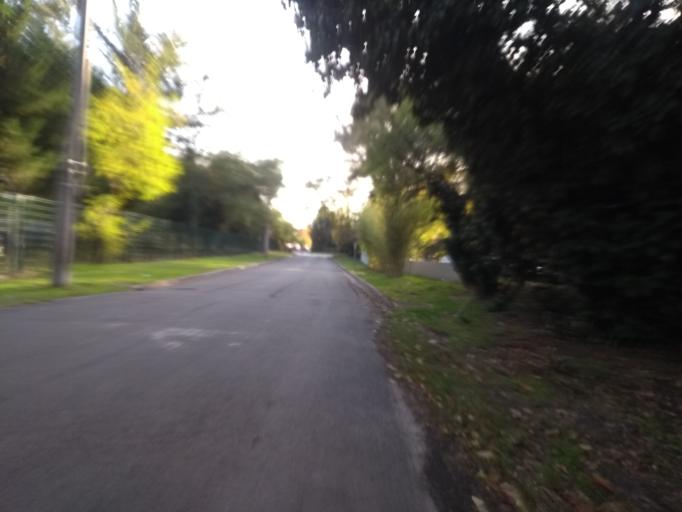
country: FR
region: Aquitaine
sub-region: Departement de la Gironde
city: Gradignan
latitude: 44.7827
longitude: -0.5985
